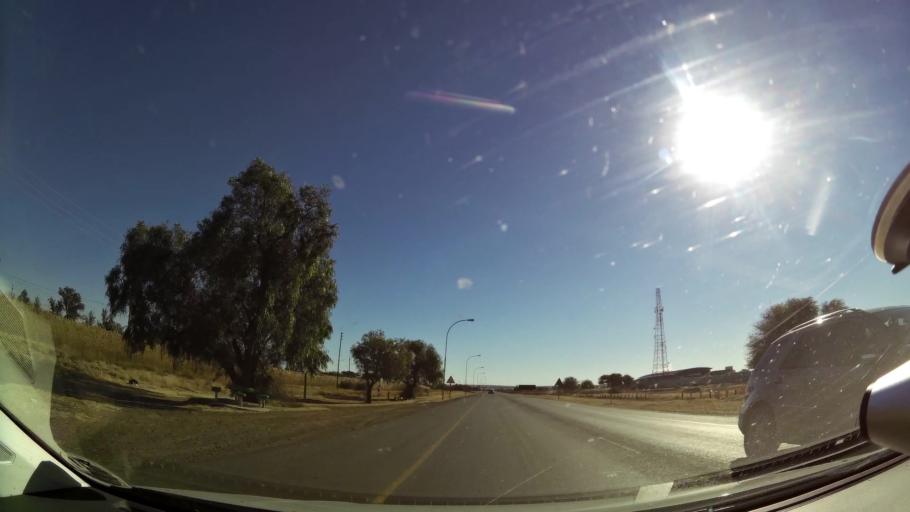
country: ZA
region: Northern Cape
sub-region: Frances Baard District Municipality
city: Kimberley
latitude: -28.7020
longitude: 24.7772
